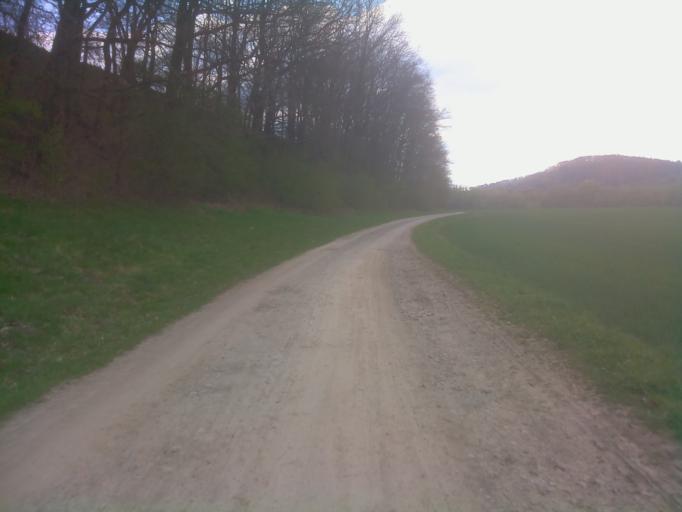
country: DE
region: Thuringia
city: Grosspurschutz
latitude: 50.8197
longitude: 11.5892
